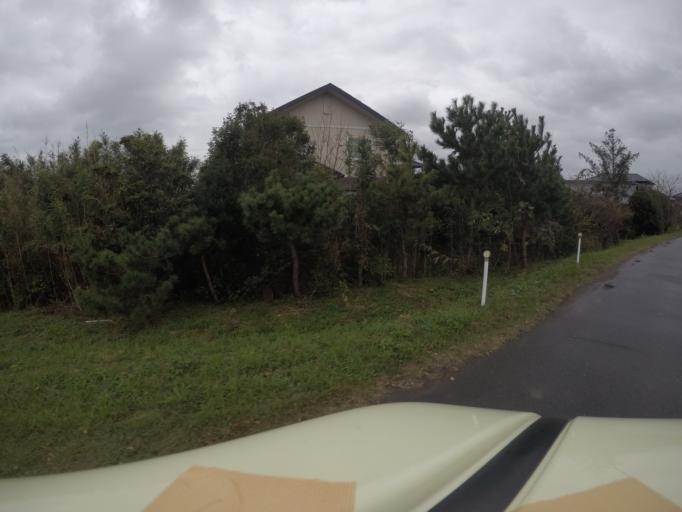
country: JP
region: Ibaraki
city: Itako
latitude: 36.0072
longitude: 140.4680
